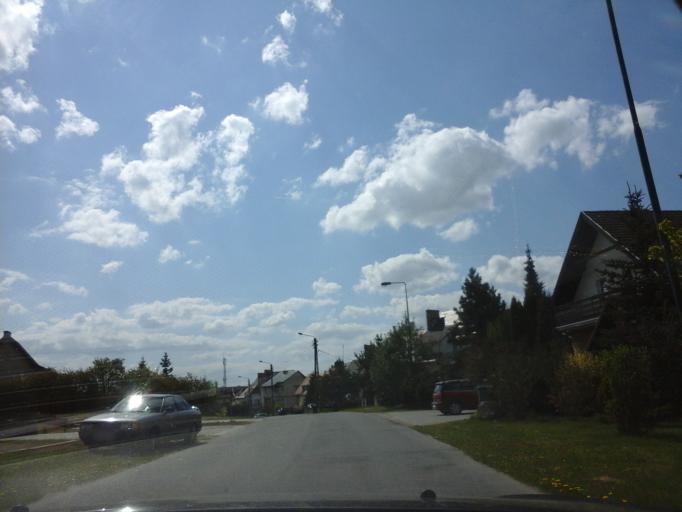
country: PL
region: West Pomeranian Voivodeship
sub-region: Powiat choszczenski
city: Choszczno
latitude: 53.1806
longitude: 15.4147
